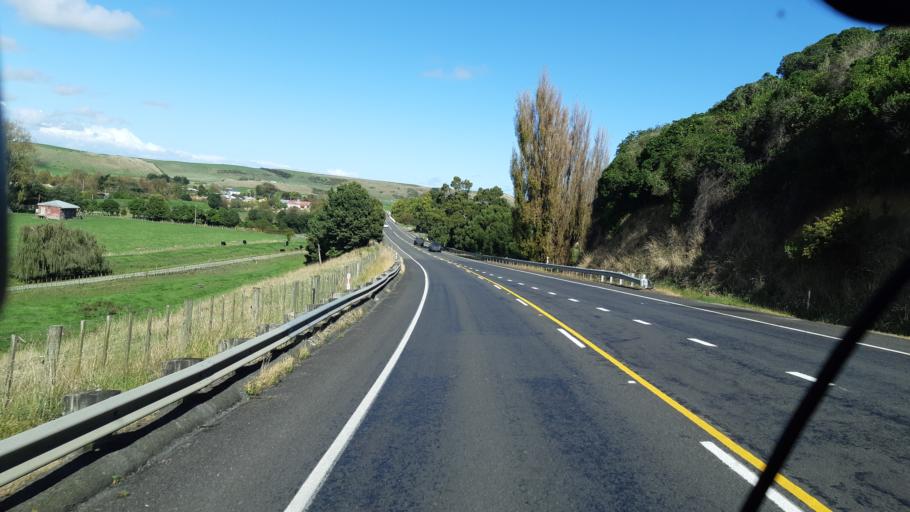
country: NZ
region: Manawatu-Wanganui
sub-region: Wanganui District
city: Wanganui
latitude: -40.0011
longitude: 175.1668
